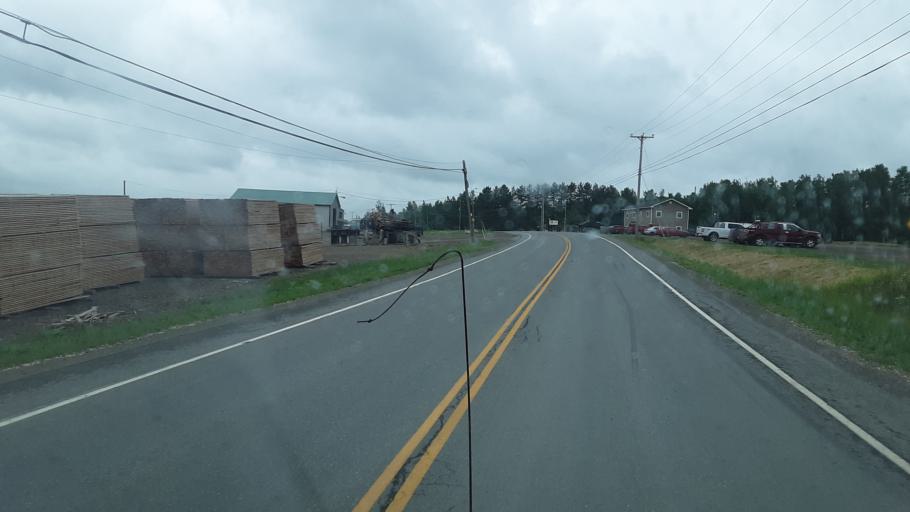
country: US
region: Maine
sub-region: Aroostook County
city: Presque Isle
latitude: 46.5308
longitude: -68.3589
